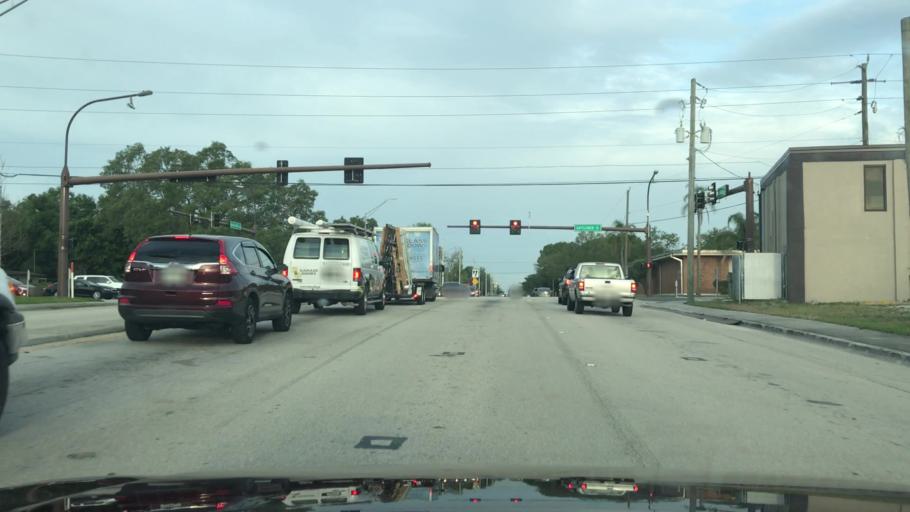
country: US
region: Florida
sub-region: Sarasota County
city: Fruitville
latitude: 27.3230
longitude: -82.4507
